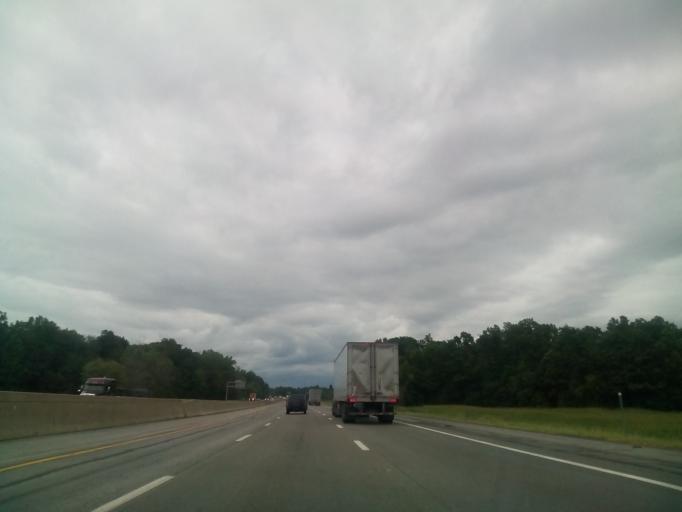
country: US
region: Ohio
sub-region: Lorain County
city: South Amherst
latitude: 41.3658
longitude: -82.2738
